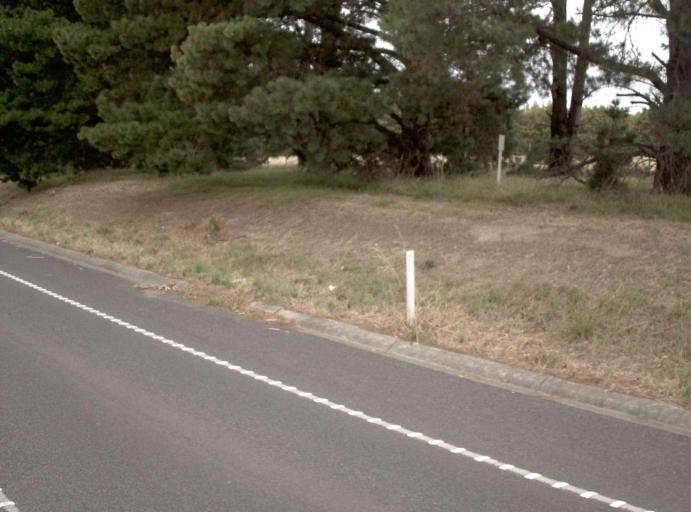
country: AU
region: Victoria
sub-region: Yarra Ranges
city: Yarra Glen
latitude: -37.6841
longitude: 145.4260
